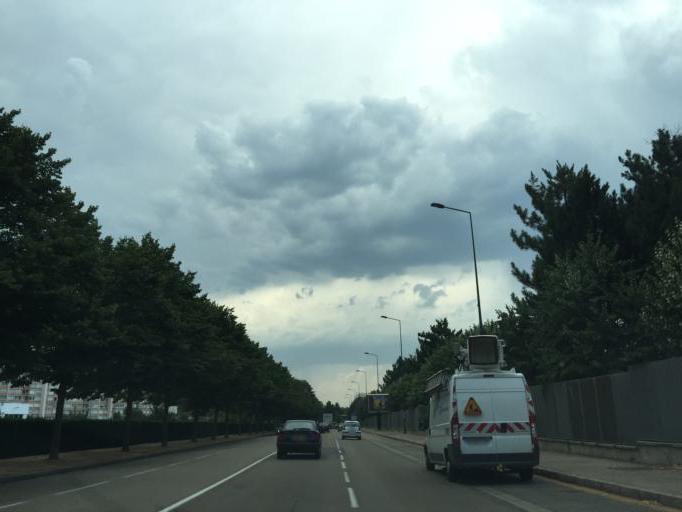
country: FR
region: Rhone-Alpes
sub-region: Departement de la Loire
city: Saint-Priest-en-Jarez
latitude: 45.4606
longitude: 4.3844
